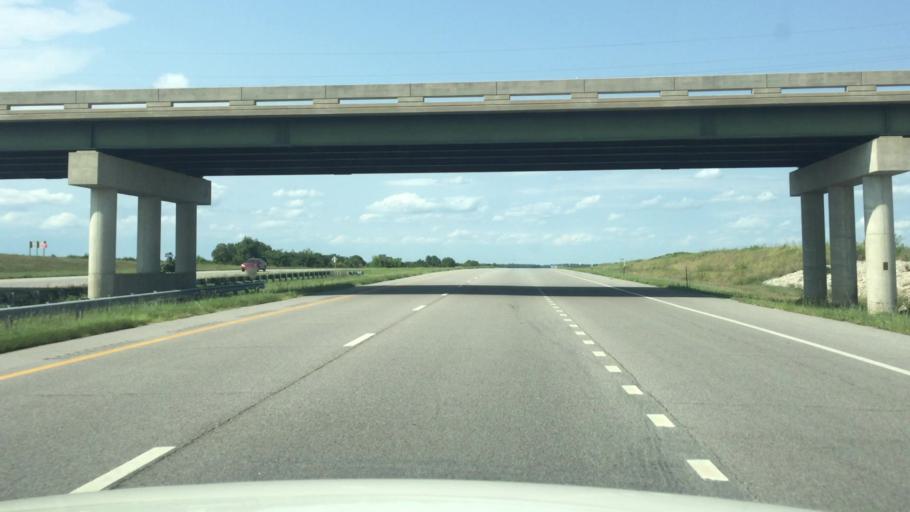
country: US
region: Kansas
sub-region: Linn County
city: La Cygne
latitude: 38.4030
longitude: -94.6877
